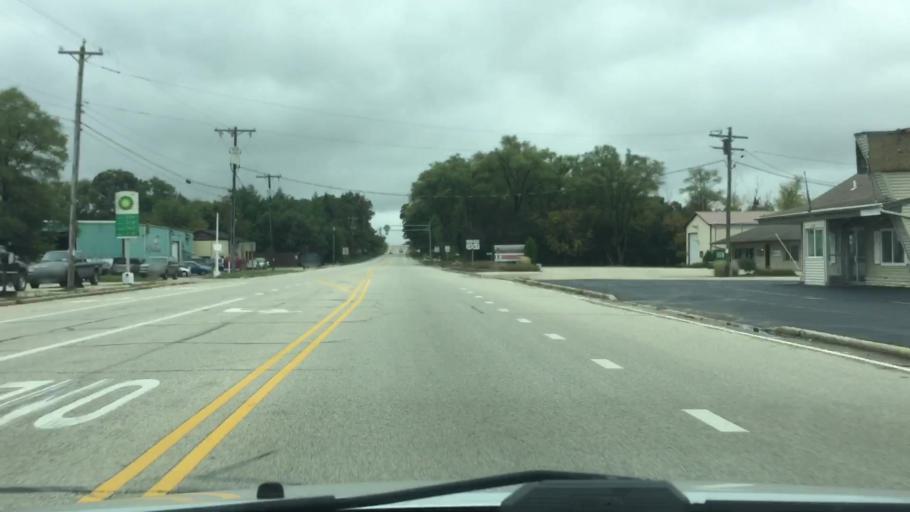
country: US
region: Wisconsin
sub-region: Walworth County
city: Elkhorn
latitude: 42.7252
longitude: -88.5428
